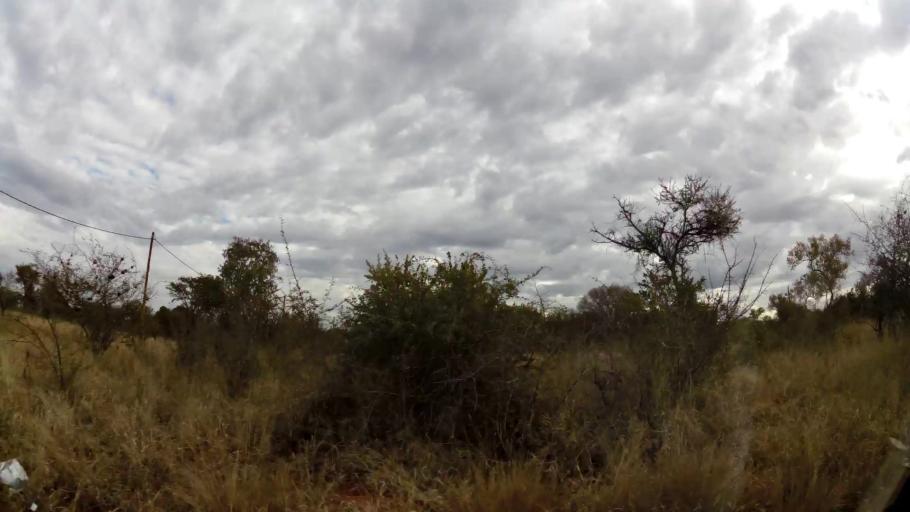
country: ZA
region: Limpopo
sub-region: Waterberg District Municipality
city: Modimolle
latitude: -24.5057
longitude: 28.7268
